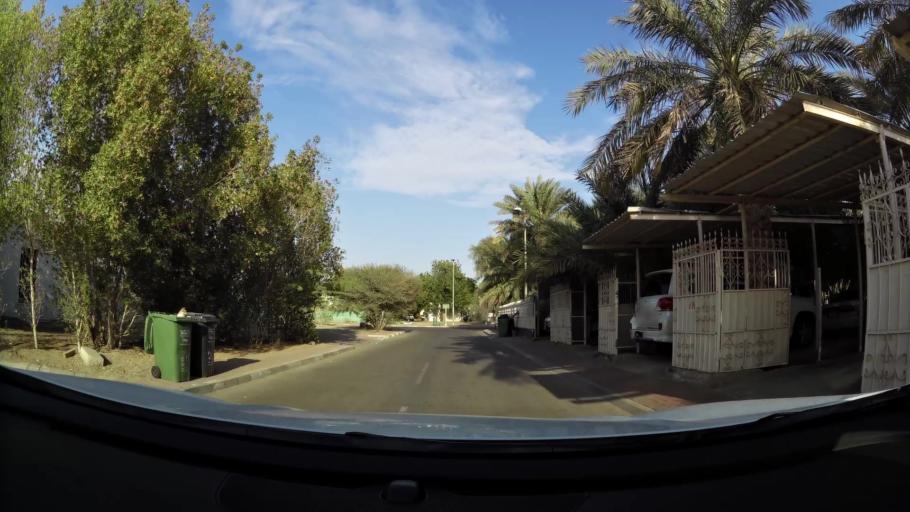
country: AE
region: Abu Dhabi
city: Al Ain
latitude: 24.0823
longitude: 55.8428
